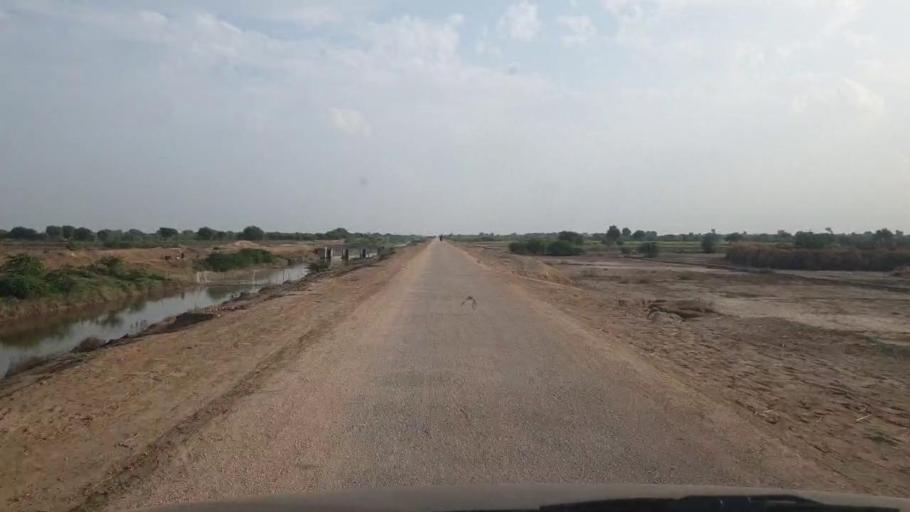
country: PK
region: Sindh
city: Badin
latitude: 24.5407
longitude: 68.6742
